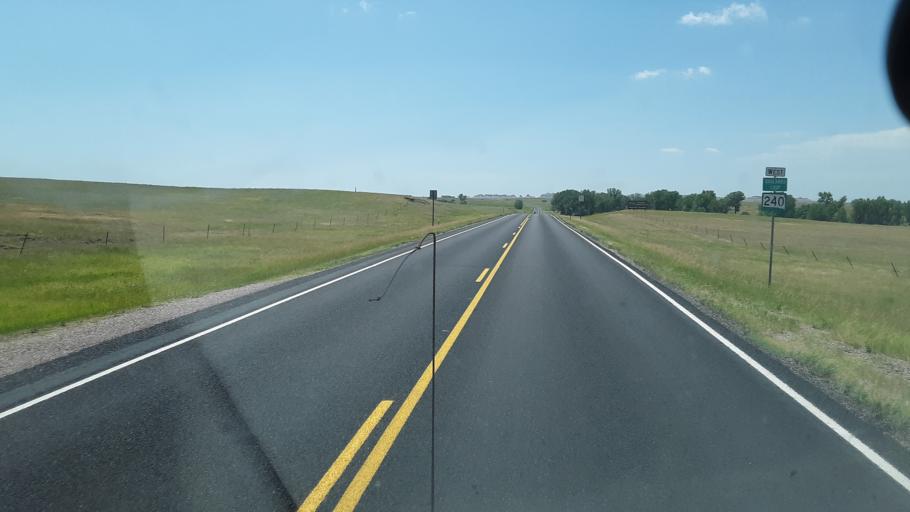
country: US
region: South Dakota
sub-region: Haakon County
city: Philip
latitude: 43.8067
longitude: -101.9019
